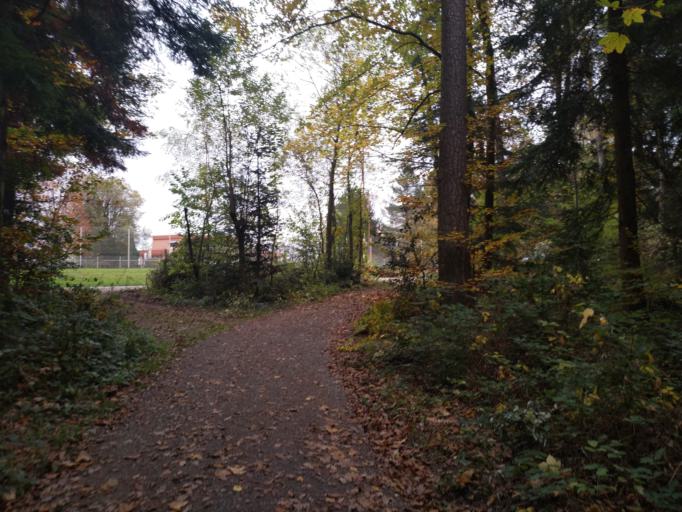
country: DE
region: Baden-Wuerttemberg
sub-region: Karlsruhe Region
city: Birkenfeld
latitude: 48.8553
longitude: 8.6510
